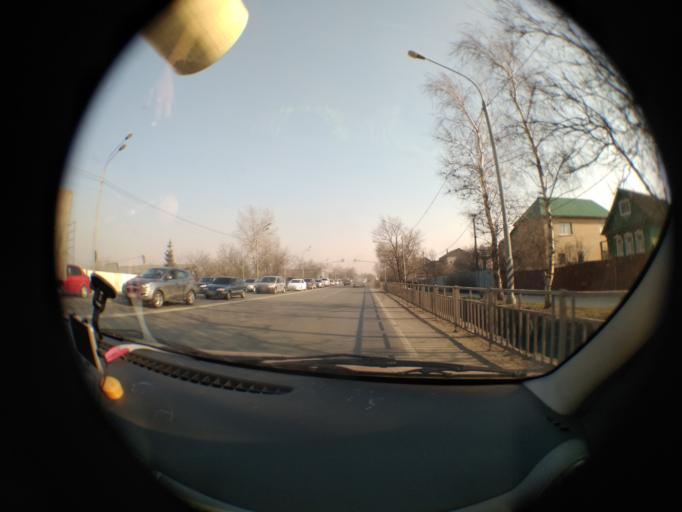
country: RU
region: Moskovskaya
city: Ostrovtsy
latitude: 55.5886
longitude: 38.0076
